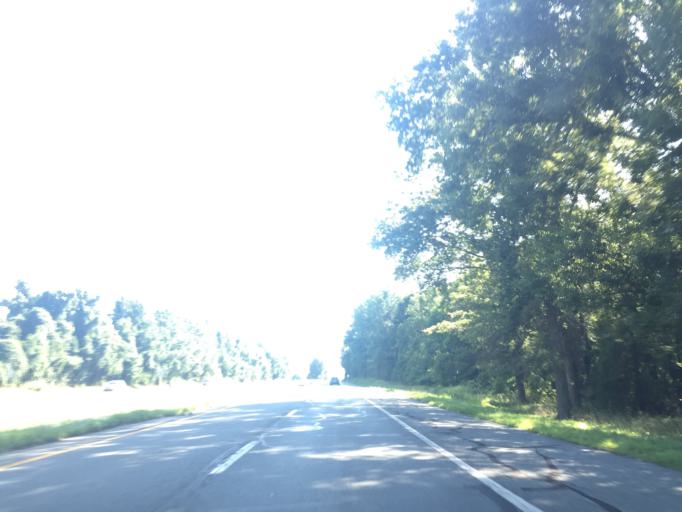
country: US
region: Maryland
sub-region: Harford County
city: North Bel Air
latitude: 39.5189
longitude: -76.3741
